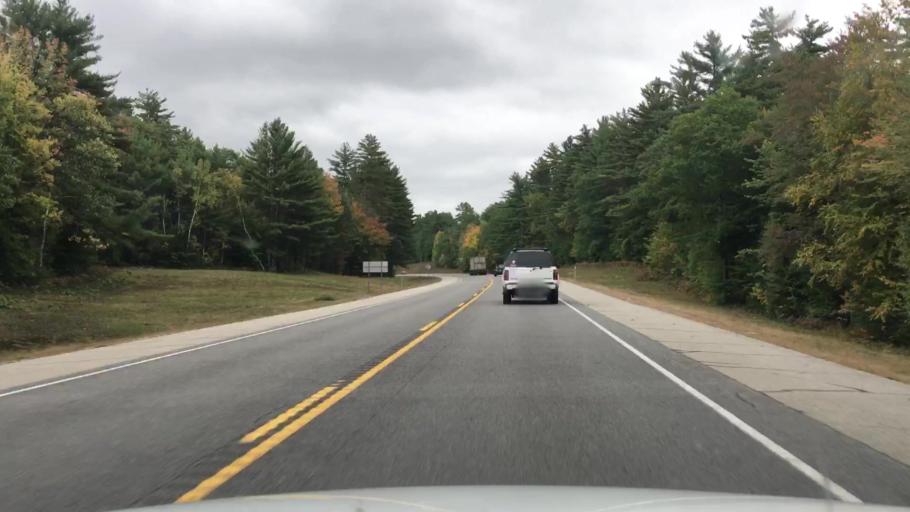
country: US
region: New Hampshire
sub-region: Carroll County
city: Tuftonboro
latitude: 43.7705
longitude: -71.1612
